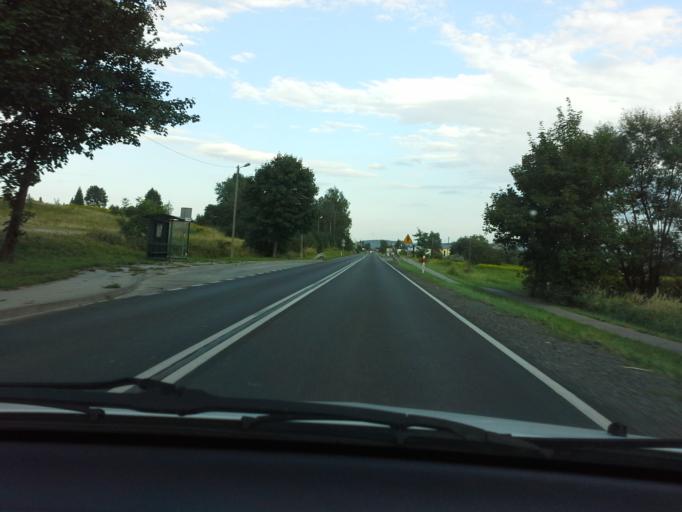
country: PL
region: Lesser Poland Voivodeship
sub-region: Powiat krakowski
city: Wola Filipowska
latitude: 50.1369
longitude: 19.5639
